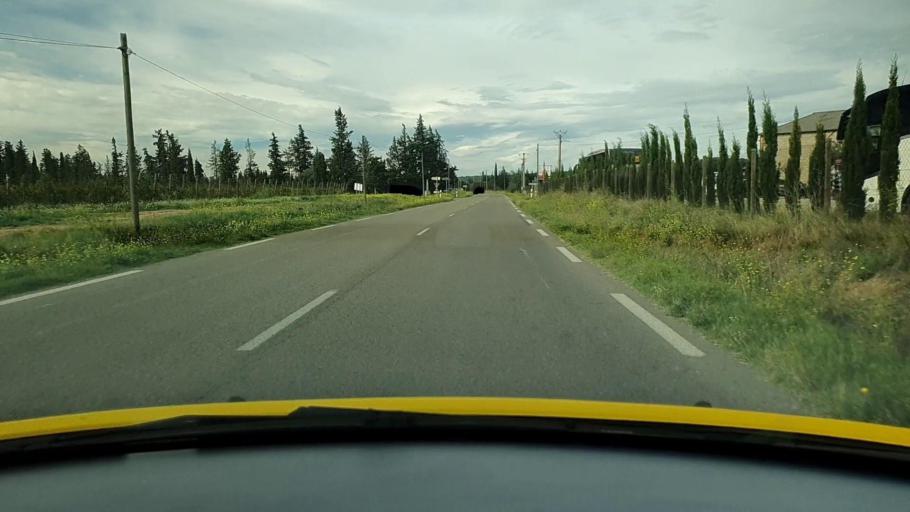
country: FR
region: Languedoc-Roussillon
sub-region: Departement du Gard
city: Jonquieres-Saint-Vincent
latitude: 43.7857
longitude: 4.5716
